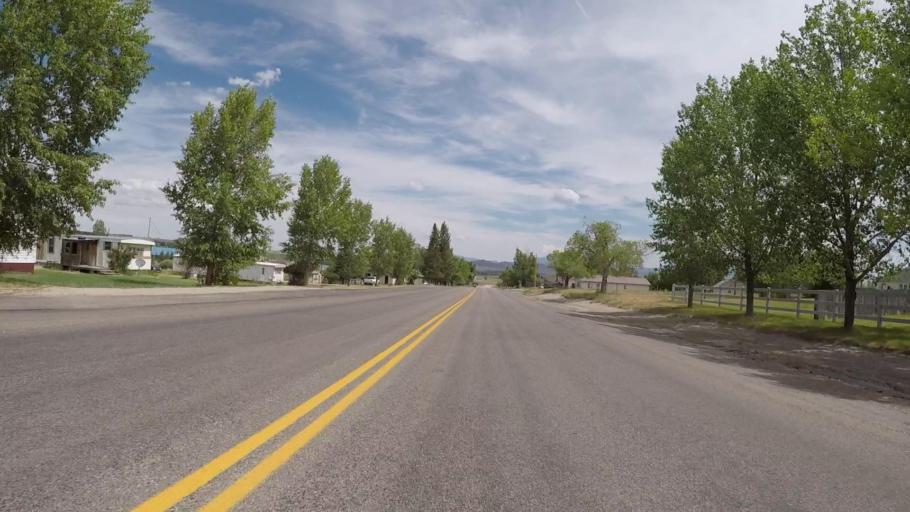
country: US
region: Wyoming
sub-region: Carbon County
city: Saratoga
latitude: 41.2069
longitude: -106.7974
